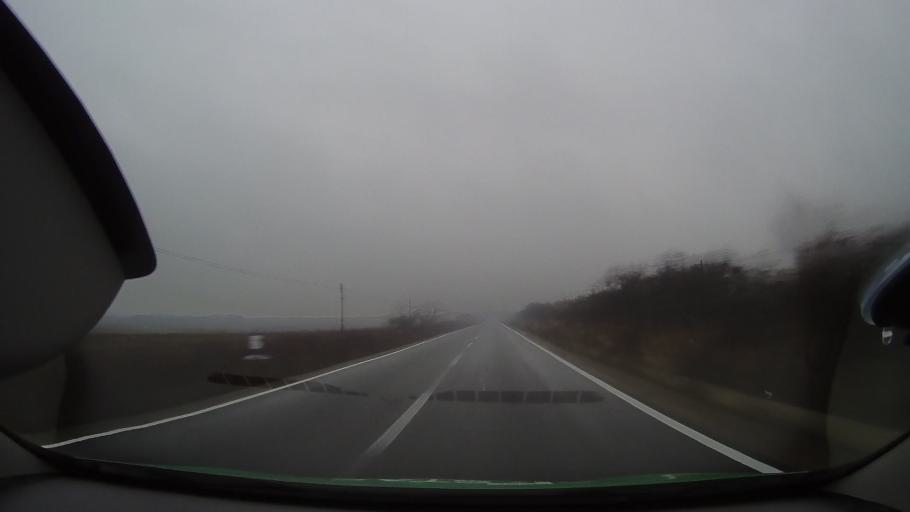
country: RO
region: Bihor
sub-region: Comuna Olcea
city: Calacea
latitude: 46.7238
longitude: 21.9474
